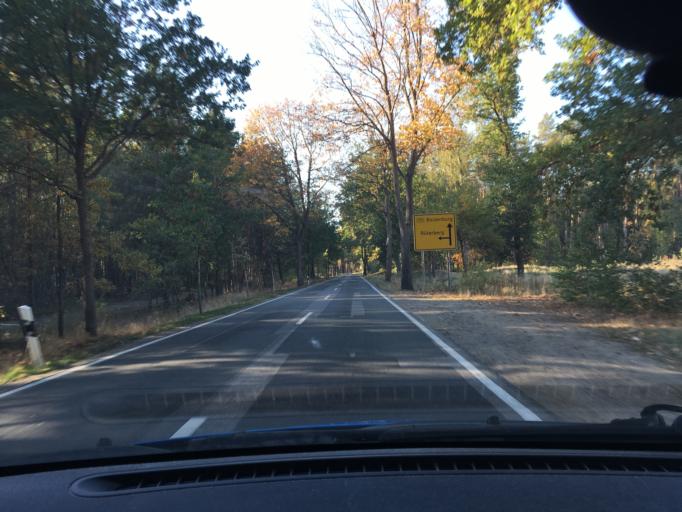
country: DE
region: Lower Saxony
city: Damnatz
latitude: 53.1582
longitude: 11.2023
